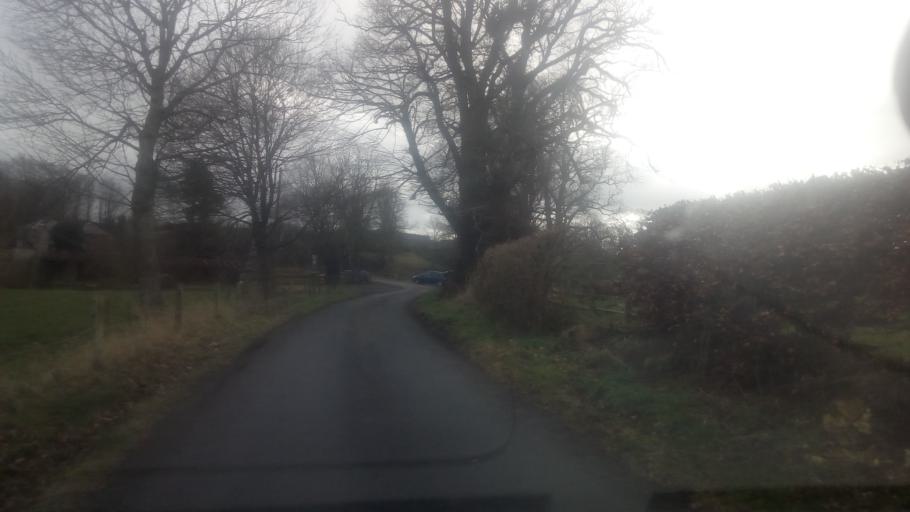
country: GB
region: Scotland
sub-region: The Scottish Borders
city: Kelso
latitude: 55.5407
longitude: -2.4647
